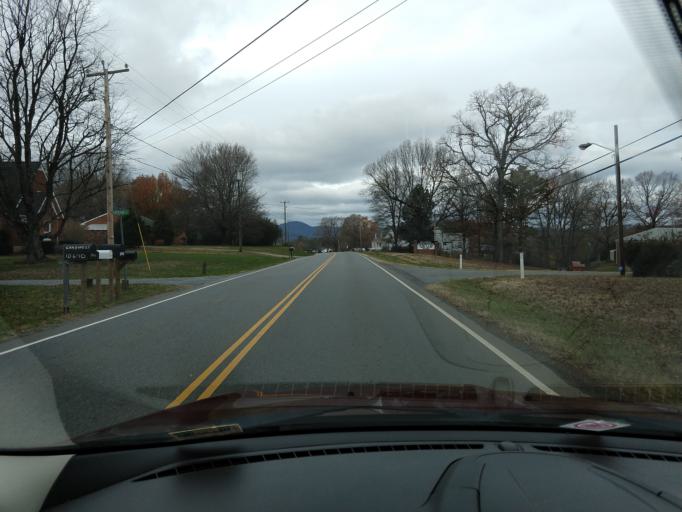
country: US
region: Virginia
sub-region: Botetourt County
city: Blue Ridge
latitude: 37.2590
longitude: -79.7263
